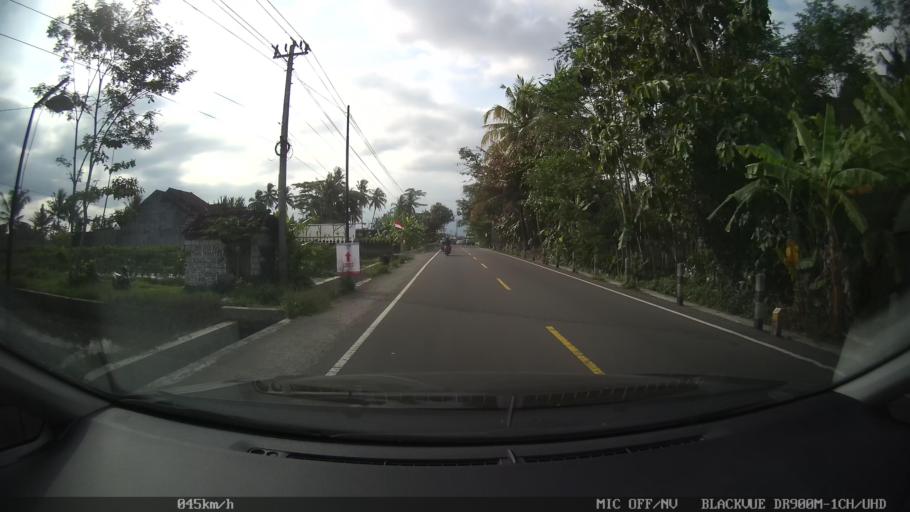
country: ID
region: Central Java
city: Candi Prambanan
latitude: -7.6882
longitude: 110.4614
